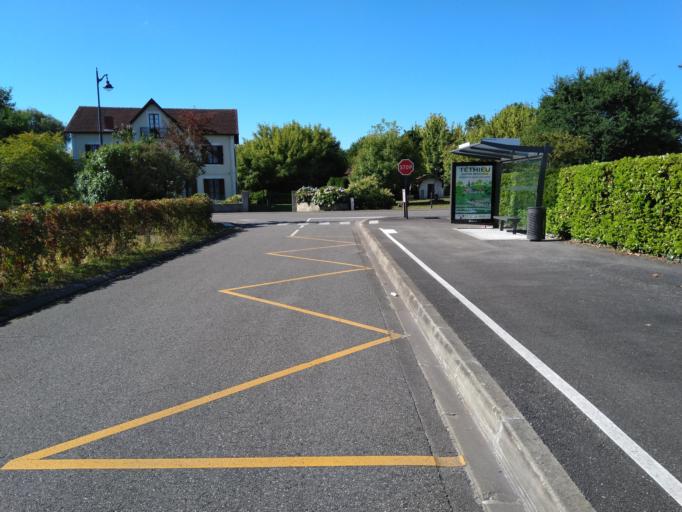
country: FR
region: Aquitaine
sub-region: Departement des Landes
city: Saint-Vincent-de-Paul
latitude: 43.7816
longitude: -0.9937
